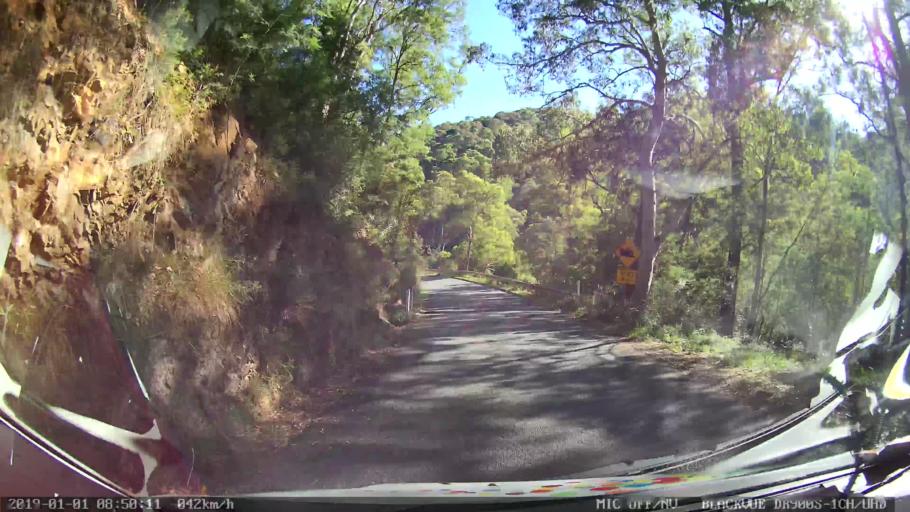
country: AU
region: New South Wales
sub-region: Snowy River
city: Jindabyne
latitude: -36.2778
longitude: 148.2024
